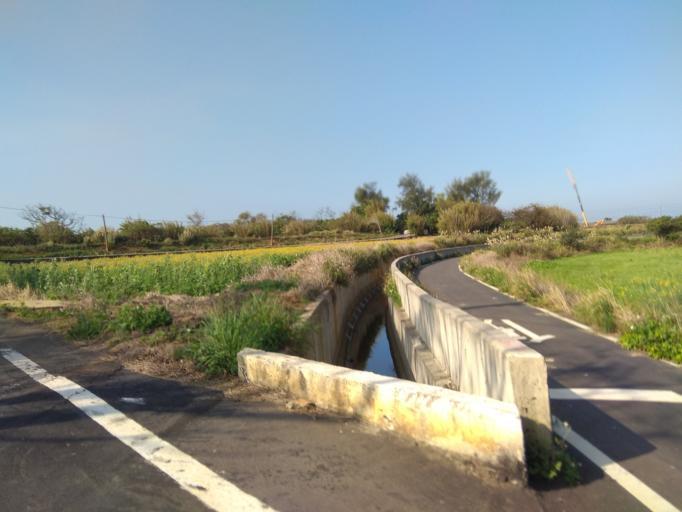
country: TW
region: Taiwan
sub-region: Hsinchu
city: Zhubei
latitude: 24.9932
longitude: 121.0374
